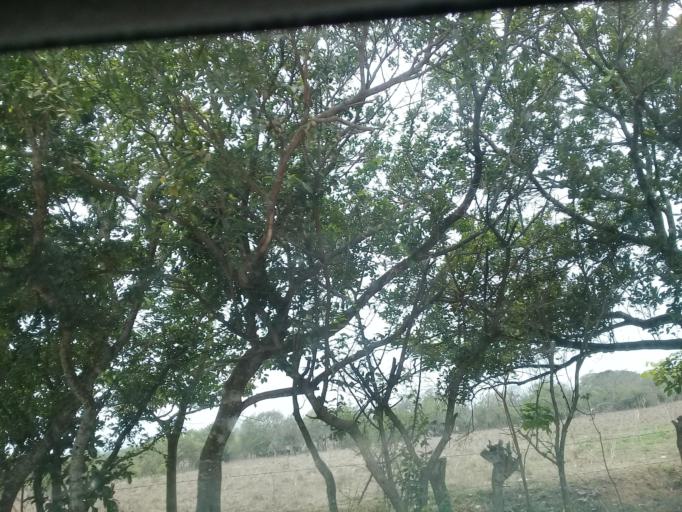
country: MX
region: Veracruz
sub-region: Veracruz
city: Las Amapolas
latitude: 19.1409
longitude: -96.2091
